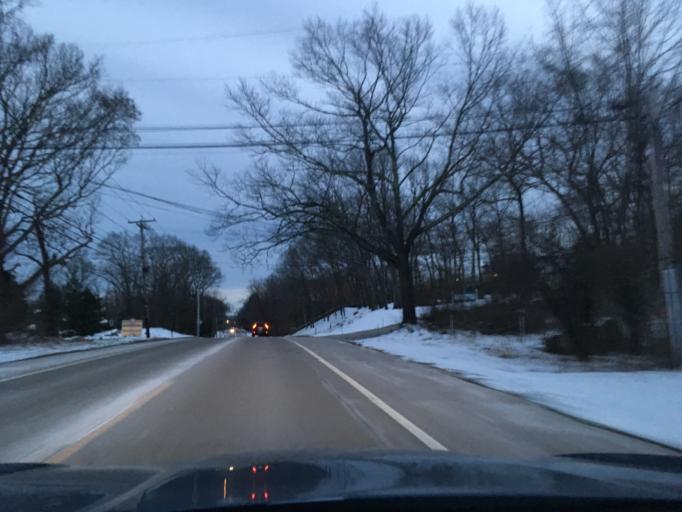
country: US
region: Rhode Island
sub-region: Kent County
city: East Greenwich
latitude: 41.6546
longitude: -71.4970
